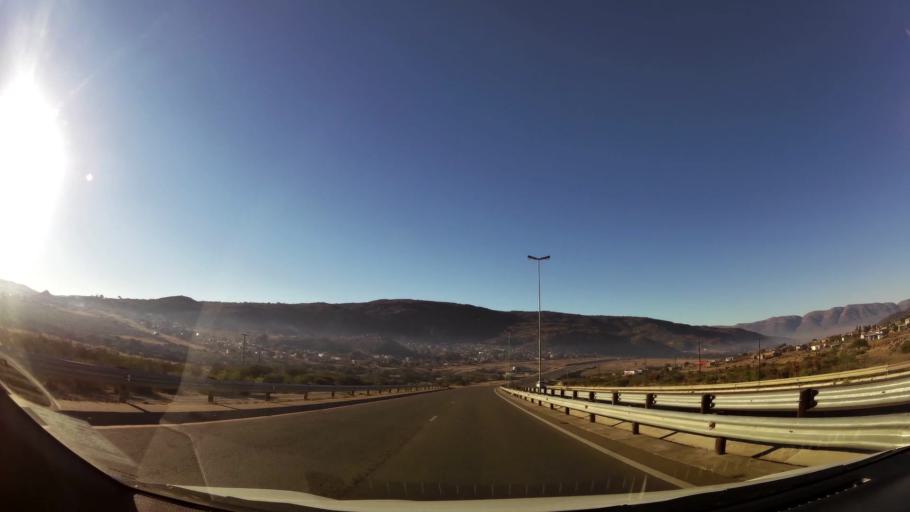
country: ZA
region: Limpopo
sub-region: Capricorn District Municipality
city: Mankoeng
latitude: -23.9154
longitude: 29.7896
